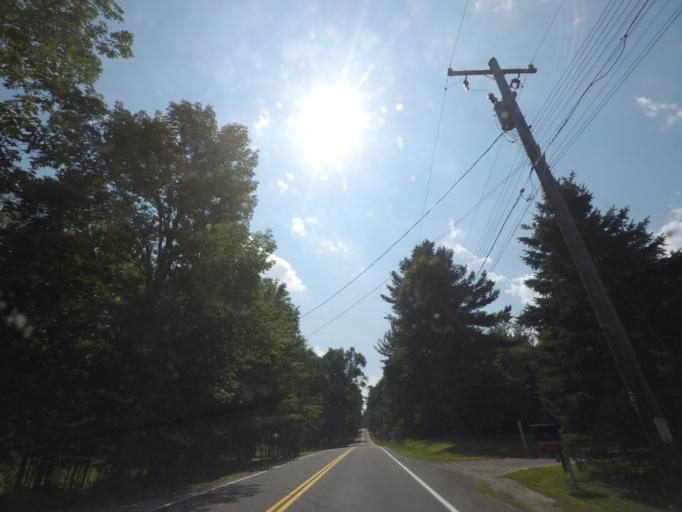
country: US
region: New York
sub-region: Rensselaer County
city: Poestenkill
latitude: 42.8054
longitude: -73.5201
